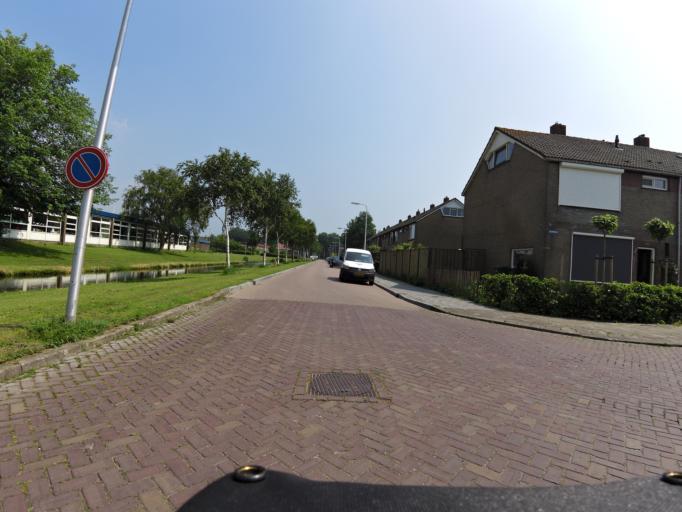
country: NL
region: South Holland
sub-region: Gemeente Maassluis
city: Maassluis
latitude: 51.8651
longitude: 4.2379
